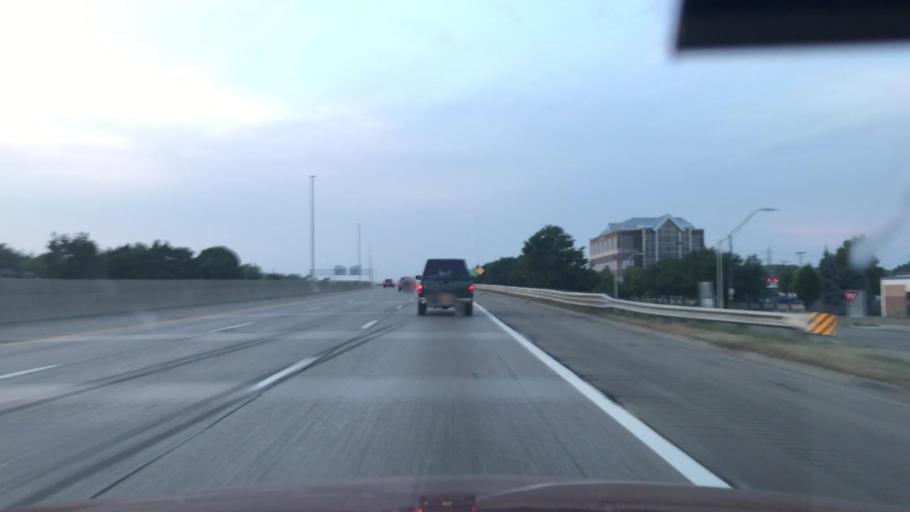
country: US
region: Michigan
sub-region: Kent County
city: Grand Rapids
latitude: 42.9823
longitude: -85.6770
